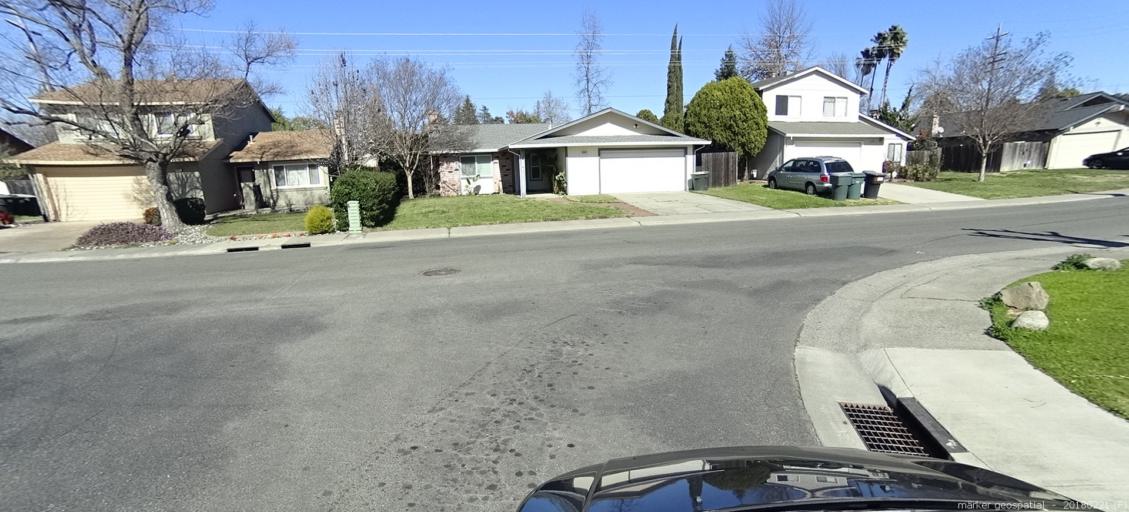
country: US
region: California
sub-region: Sacramento County
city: Orangevale
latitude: 38.6927
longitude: -121.2509
